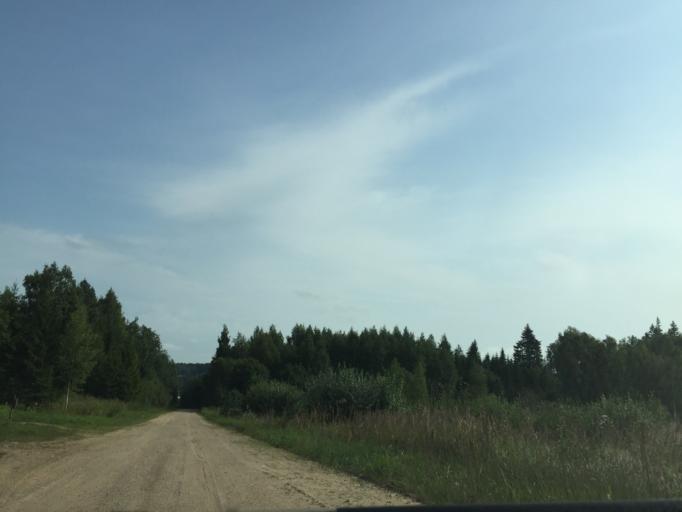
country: LV
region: Dagda
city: Dagda
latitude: 56.2912
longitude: 27.6337
